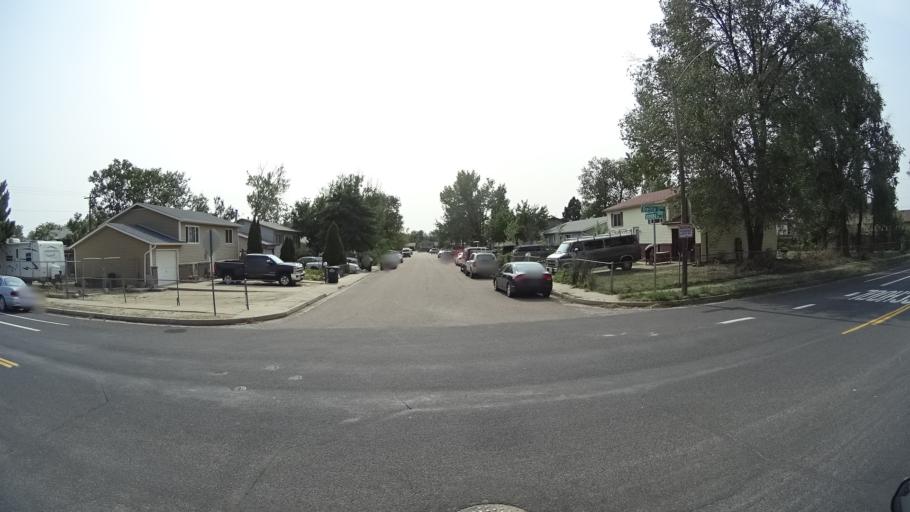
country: US
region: Colorado
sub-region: El Paso County
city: Stratmoor
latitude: 38.7958
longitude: -104.7664
